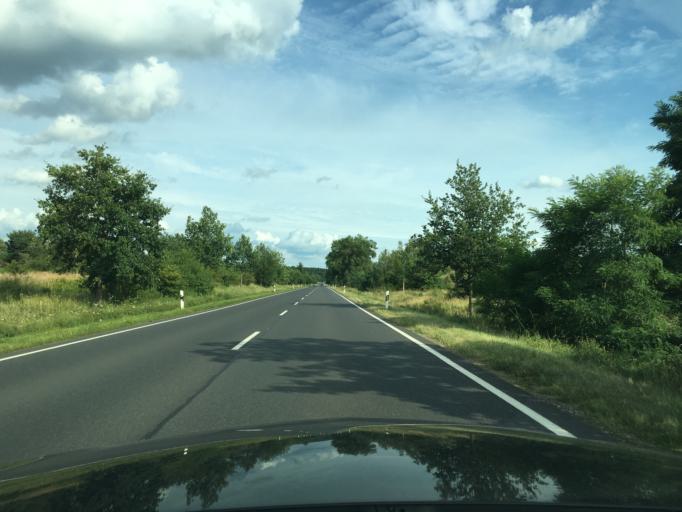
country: DE
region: Mecklenburg-Vorpommern
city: Neustrelitz
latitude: 53.3823
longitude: 13.0553
